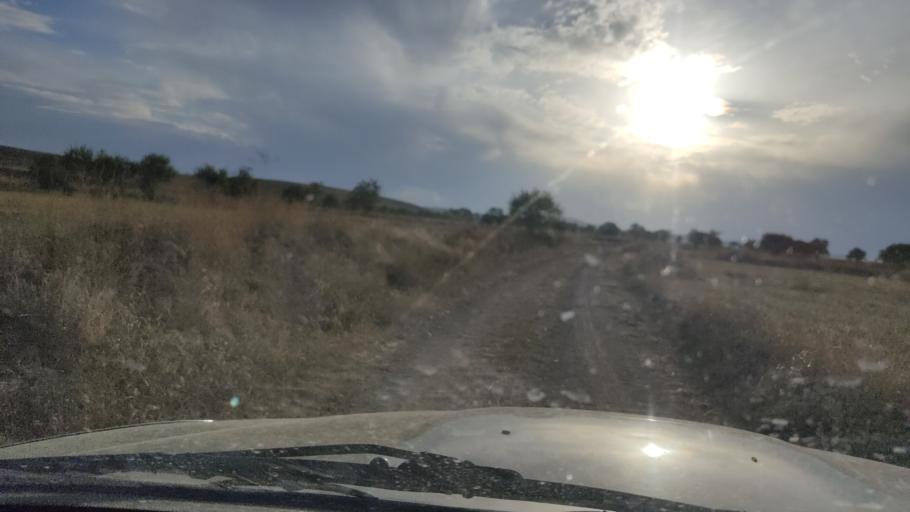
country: ES
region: Aragon
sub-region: Provincia de Teruel
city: Monforte de Moyuela
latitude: 41.0659
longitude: -0.9822
